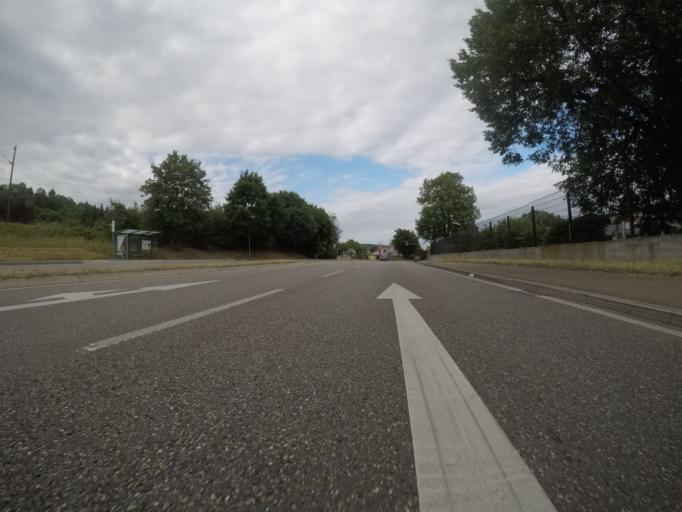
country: DE
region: Baden-Wuerttemberg
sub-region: Karlsruhe Region
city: Eutingen
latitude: 48.9035
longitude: 8.7350
